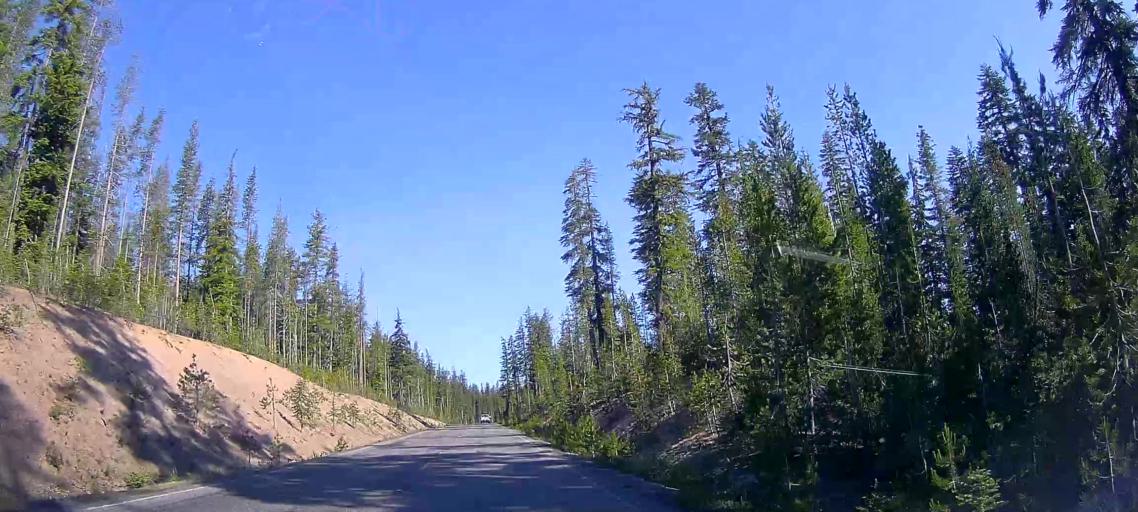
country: US
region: Oregon
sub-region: Jackson County
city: Shady Cove
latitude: 42.8501
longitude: -122.1487
